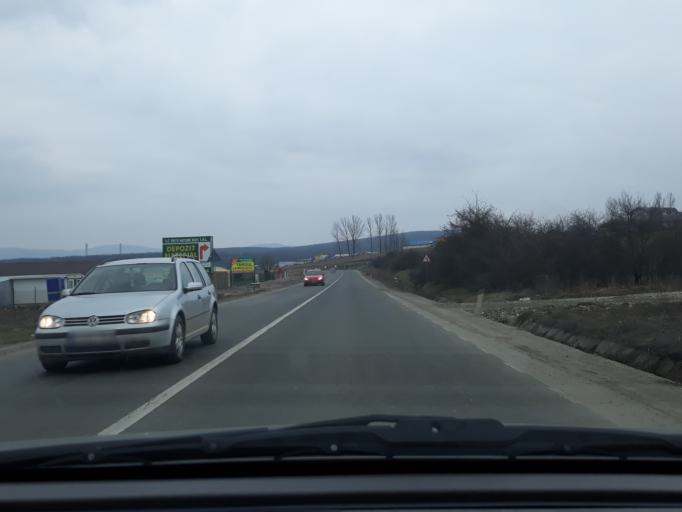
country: RO
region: Salaj
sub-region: Comuna Hereclean
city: Hereclean
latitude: 47.2321
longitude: 22.9970
